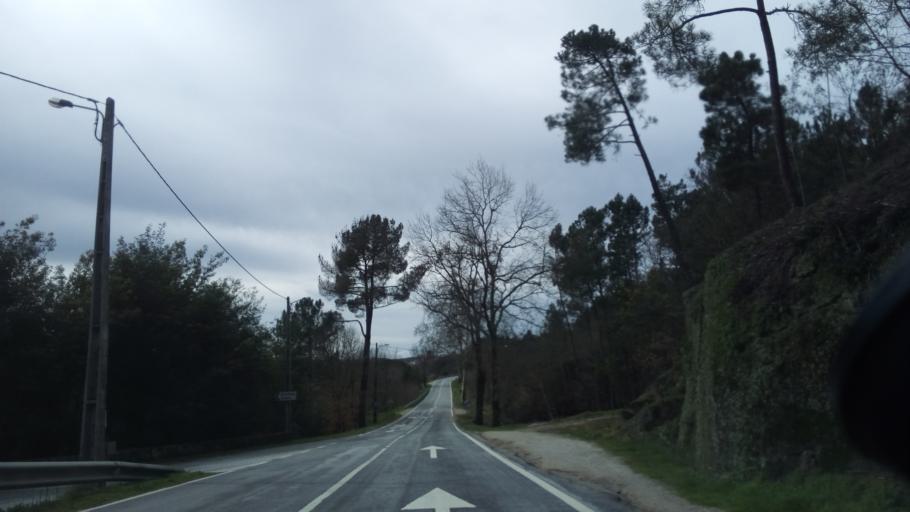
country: PT
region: Guarda
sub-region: Seia
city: Seia
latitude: 40.4364
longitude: -7.7113
